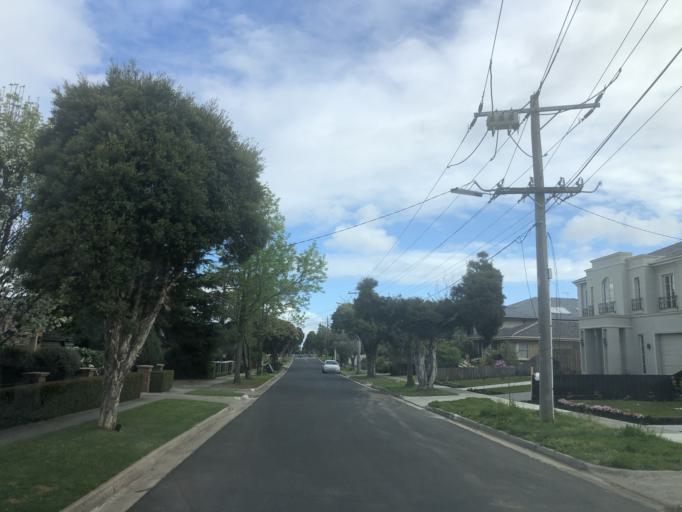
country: AU
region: Victoria
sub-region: Monash
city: Ashwood
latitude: -37.8782
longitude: 145.1156
